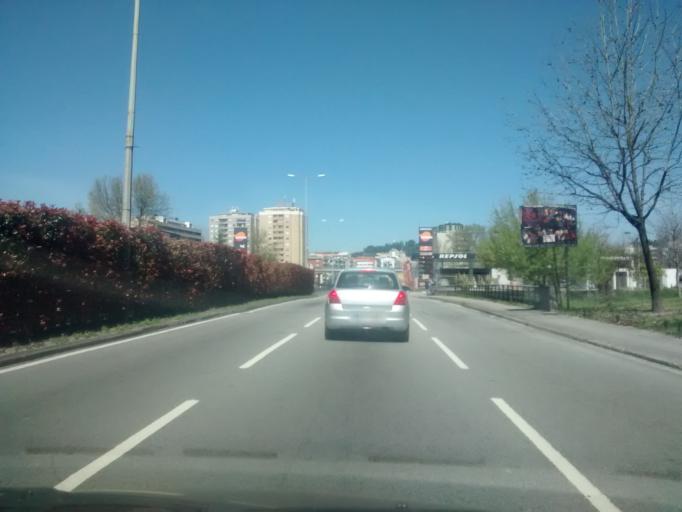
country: PT
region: Braga
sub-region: Braga
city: Braga
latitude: 41.5502
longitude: -8.4058
